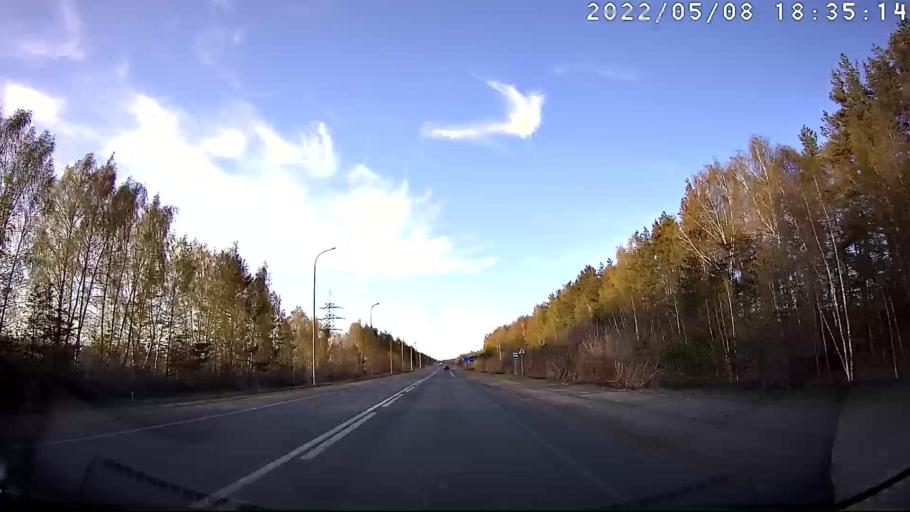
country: RU
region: Mariy-El
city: Volzhsk
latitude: 55.9072
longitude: 48.3607
